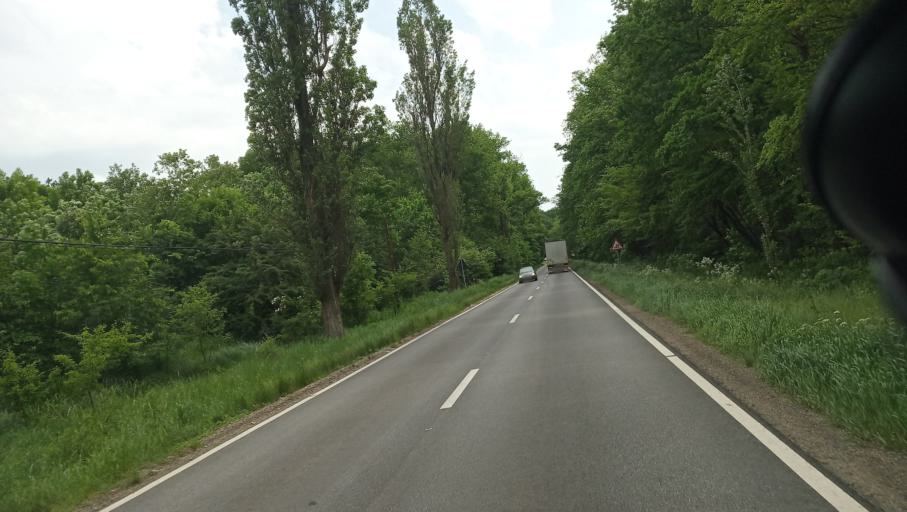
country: RO
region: Neamt
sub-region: Comuna Vanatori Neamt
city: Nemtisor
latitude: 47.2339
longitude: 26.2275
